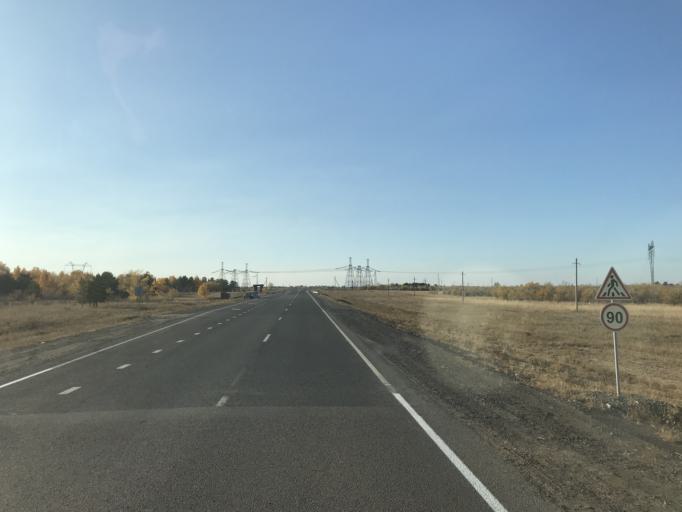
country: KZ
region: Pavlodar
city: Koktobe
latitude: 51.9068
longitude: 77.3664
